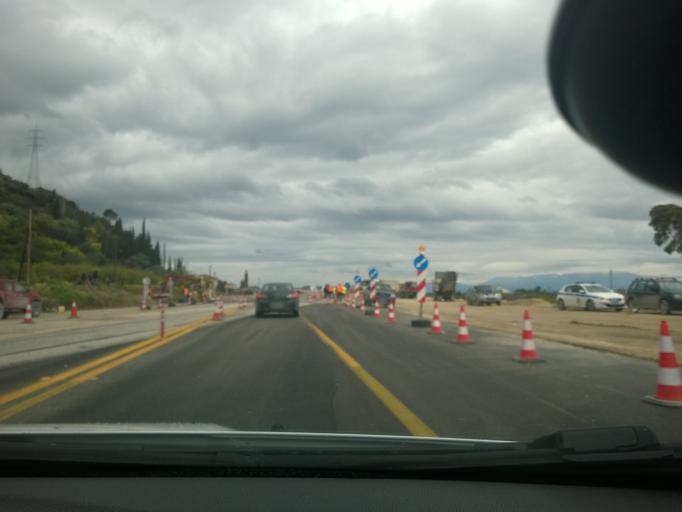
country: GR
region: Peloponnese
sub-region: Nomos Korinthias
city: Xylokastro
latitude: 38.0924
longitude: 22.5716
